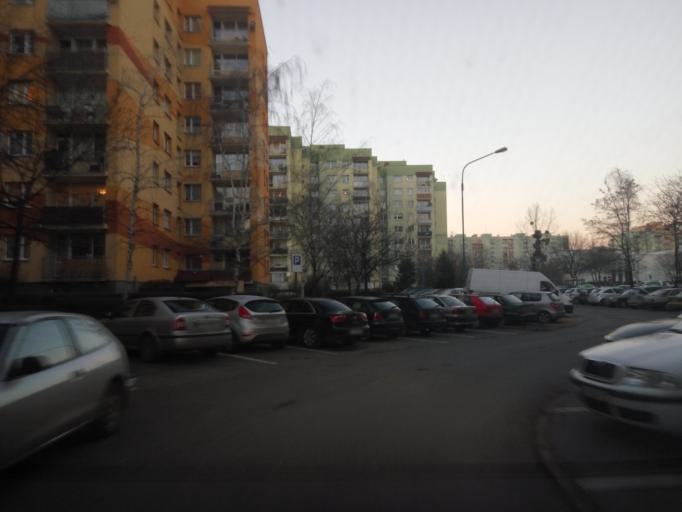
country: PL
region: Lower Silesian Voivodeship
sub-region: Powiat wroclawski
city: Bielany Wroclawskie
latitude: 51.1138
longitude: 16.9512
